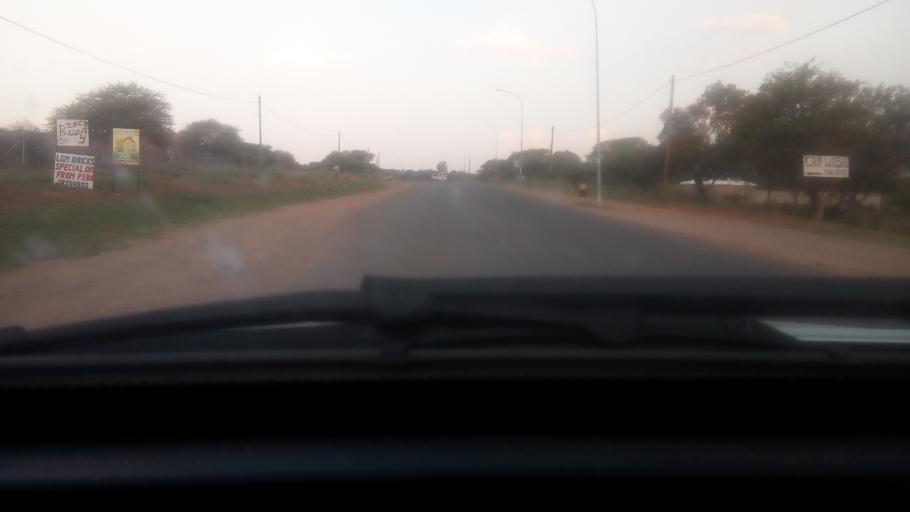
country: BW
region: Kgatleng
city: Bokaa
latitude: -24.4340
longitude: 26.0343
